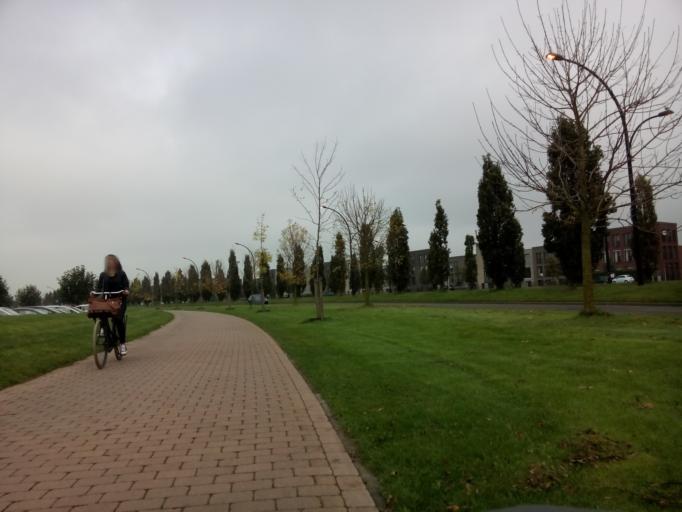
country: NL
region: Utrecht
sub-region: Gemeente Amersfoort
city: Randenbroek
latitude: 52.1962
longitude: 5.4316
